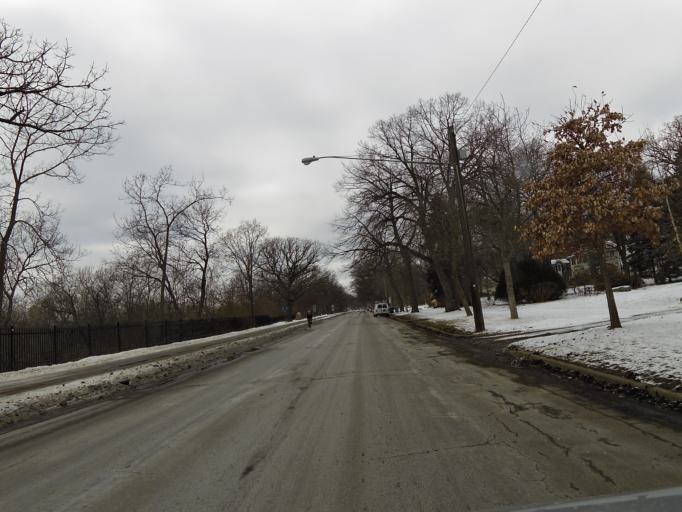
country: US
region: Minnesota
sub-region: Ramsey County
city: Lauderdale
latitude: 44.9615
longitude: -93.2161
